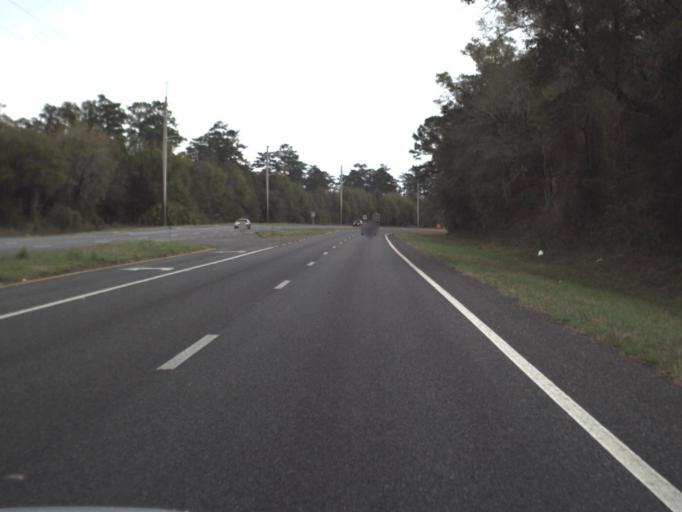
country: US
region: Florida
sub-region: Leon County
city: Woodville
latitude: 30.4130
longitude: -84.0783
